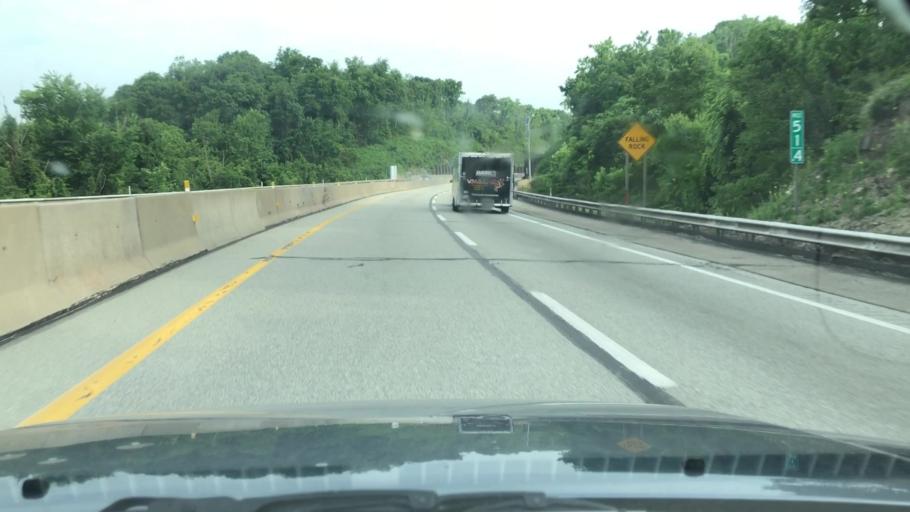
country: US
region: Pennsylvania
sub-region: Allegheny County
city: Springdale
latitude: 40.5027
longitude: -79.7882
